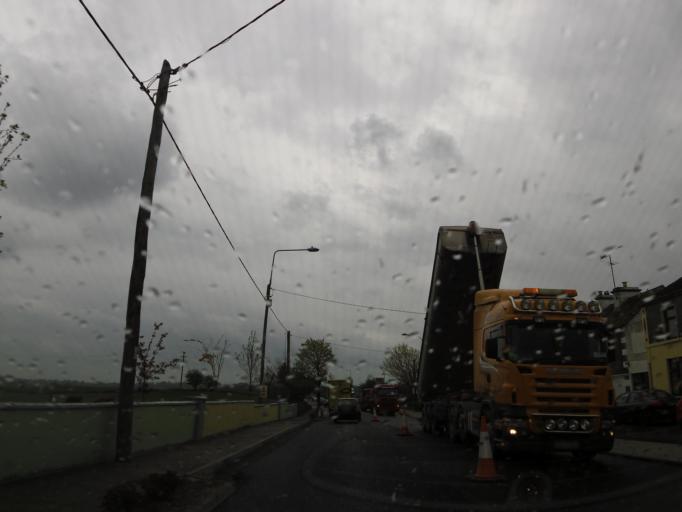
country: IE
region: Connaught
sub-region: County Galway
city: Tuam
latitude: 53.6110
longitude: -8.8963
